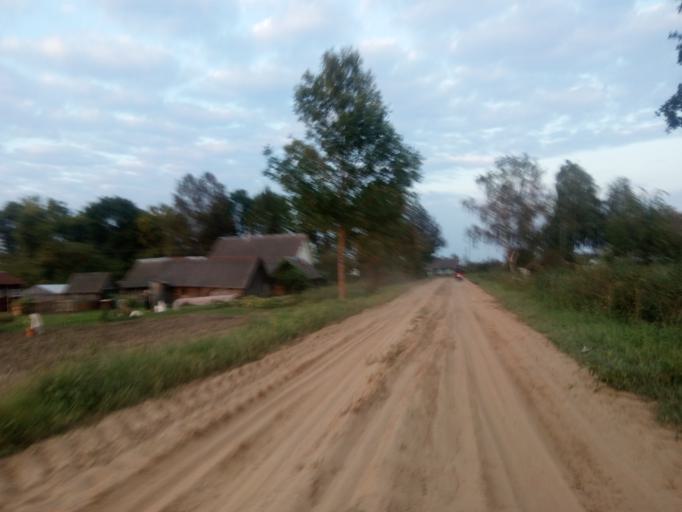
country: BY
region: Vitebsk
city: Dzisna
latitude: 55.6614
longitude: 28.3230
